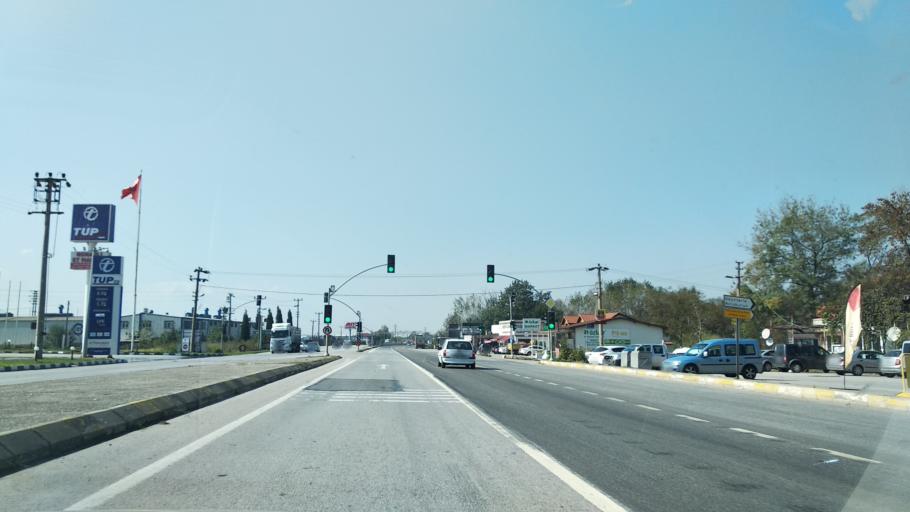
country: TR
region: Kocaeli
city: Derbent
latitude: 40.7295
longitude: 30.1440
